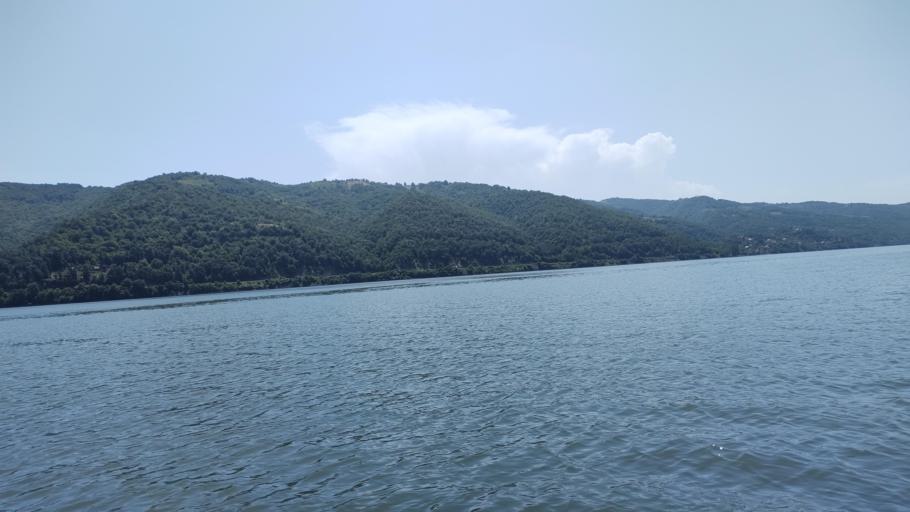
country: RO
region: Mehedinti
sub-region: Comuna Svinita
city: Svinita
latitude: 44.5197
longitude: 22.2014
